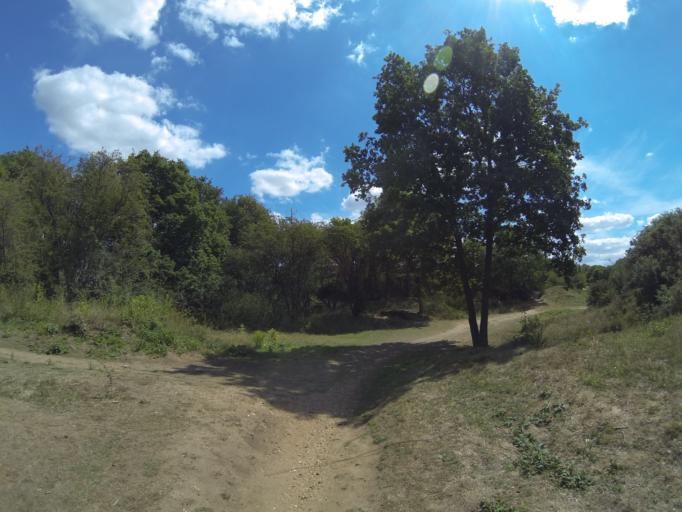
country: GB
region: England
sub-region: Greater London
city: Bexley
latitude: 51.4373
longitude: 0.1837
